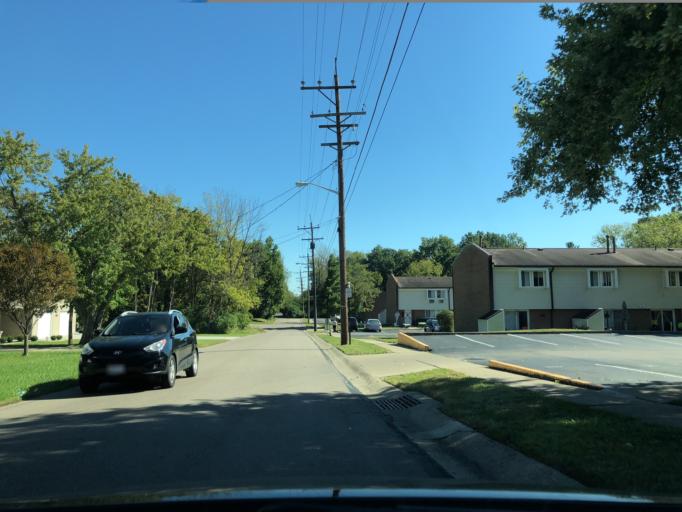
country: US
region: Ohio
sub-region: Hamilton County
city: Loveland
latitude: 39.2680
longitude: -84.2711
